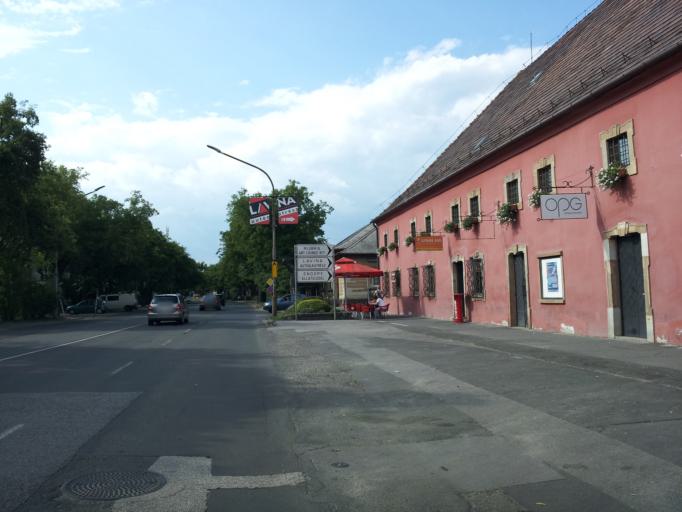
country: HU
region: Pest
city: Vac
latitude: 47.7787
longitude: 19.1342
